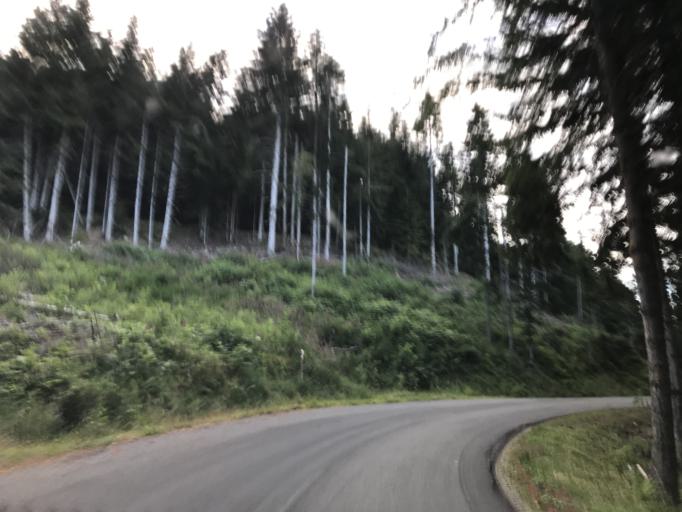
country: FR
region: Rhone-Alpes
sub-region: Departement de la Loire
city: Noiretable
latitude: 45.7548
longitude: 3.8247
